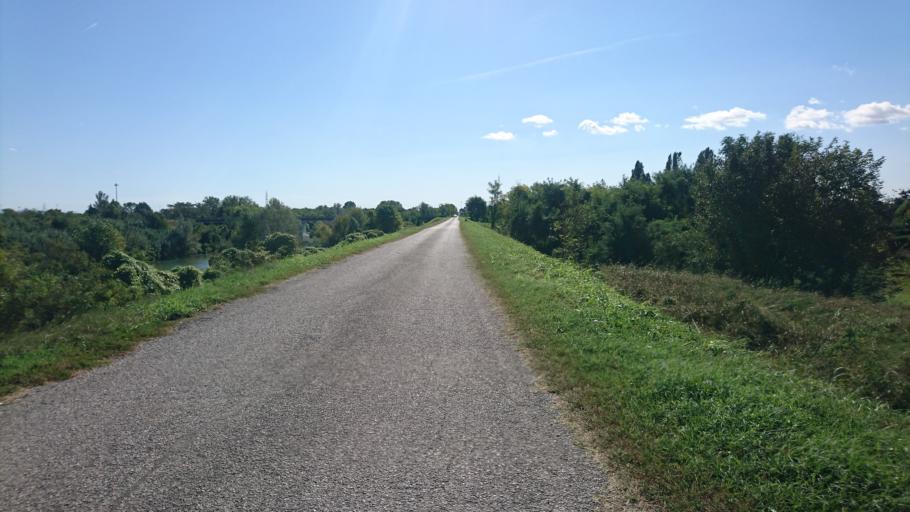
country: IT
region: Veneto
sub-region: Provincia di Venezia
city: Vigonovo
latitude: 45.3879
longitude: 12.0139
